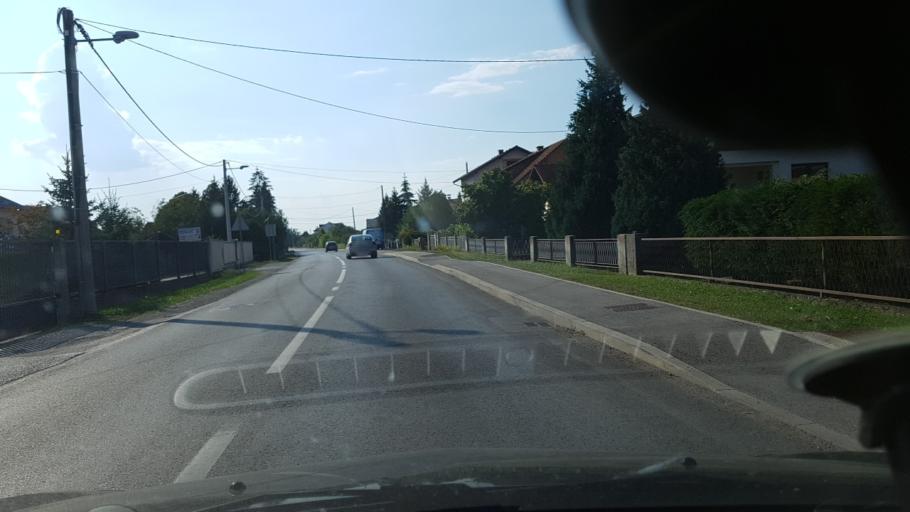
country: HR
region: Zagrebacka
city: Brdovec
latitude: 45.8785
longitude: 15.7339
